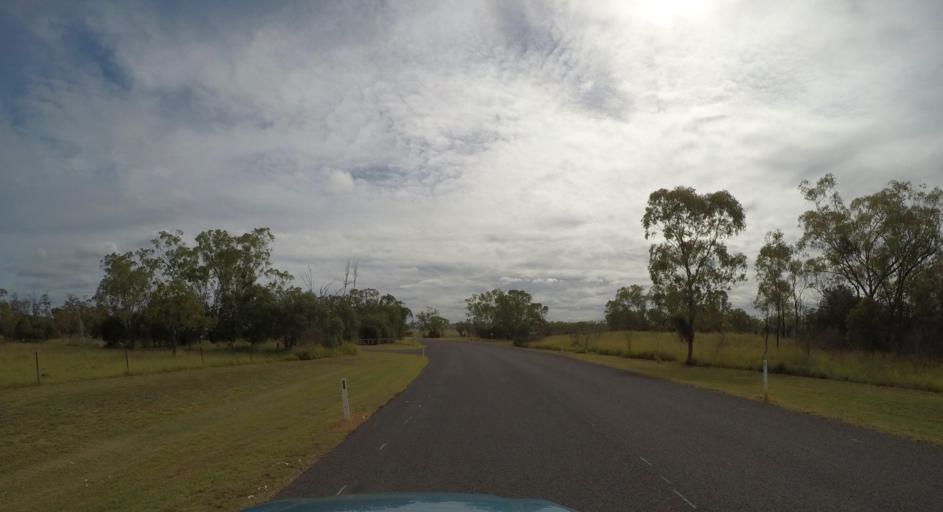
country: AU
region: Queensland
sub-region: Western Downs
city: Dalby
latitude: -27.0546
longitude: 151.3165
